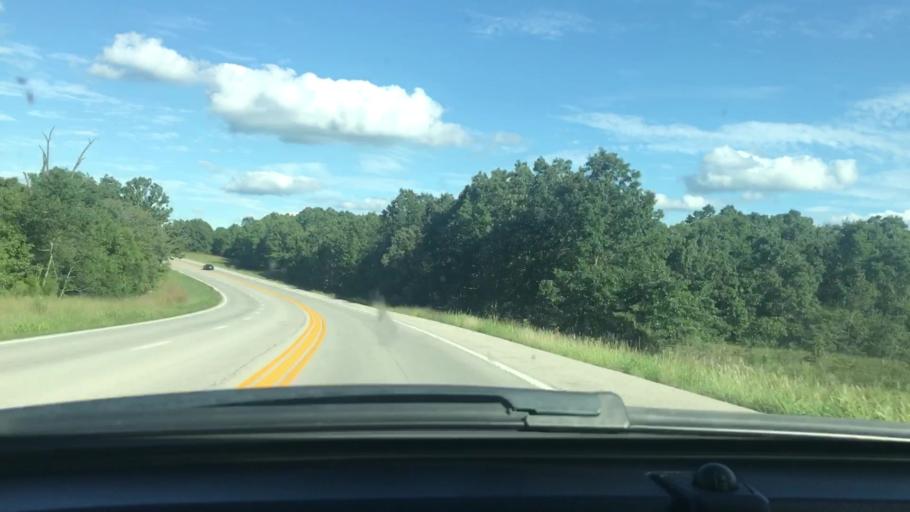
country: US
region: Missouri
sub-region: Howell County
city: West Plains
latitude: 36.6608
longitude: -91.7192
